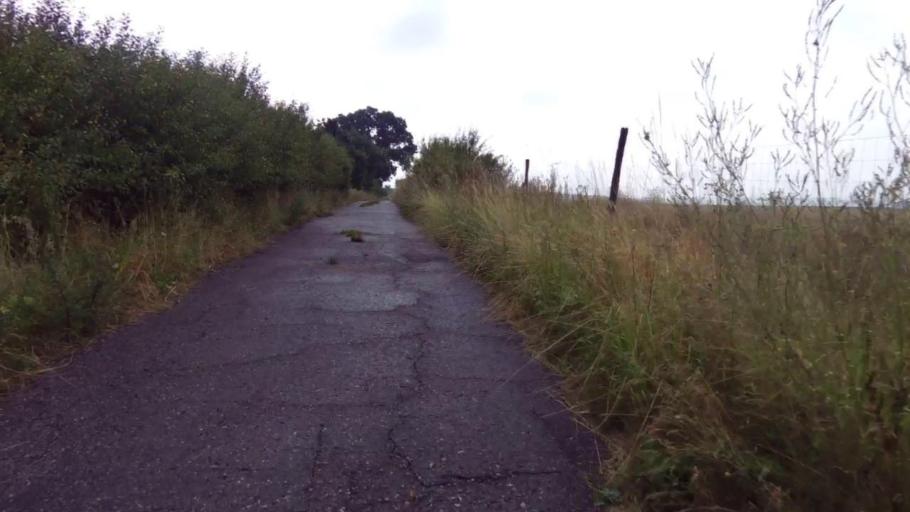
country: PL
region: West Pomeranian Voivodeship
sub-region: Powiat choszczenski
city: Recz
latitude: 53.2561
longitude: 15.4621
